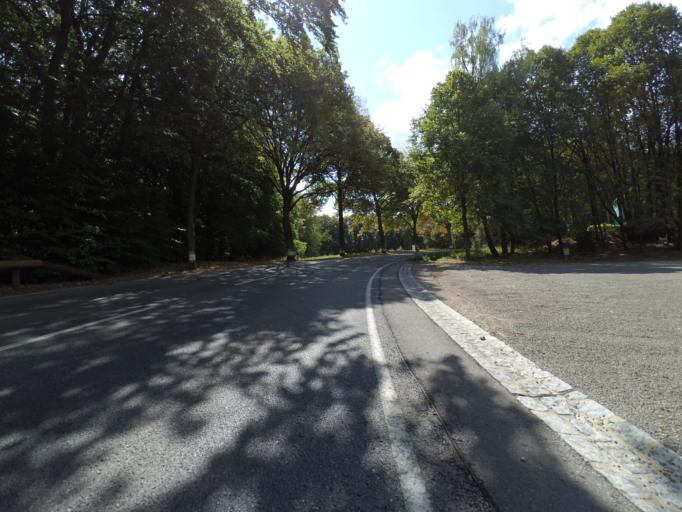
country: LU
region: Luxembourg
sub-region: Canton de Luxembourg
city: Niederanven
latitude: 49.6589
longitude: 6.2295
